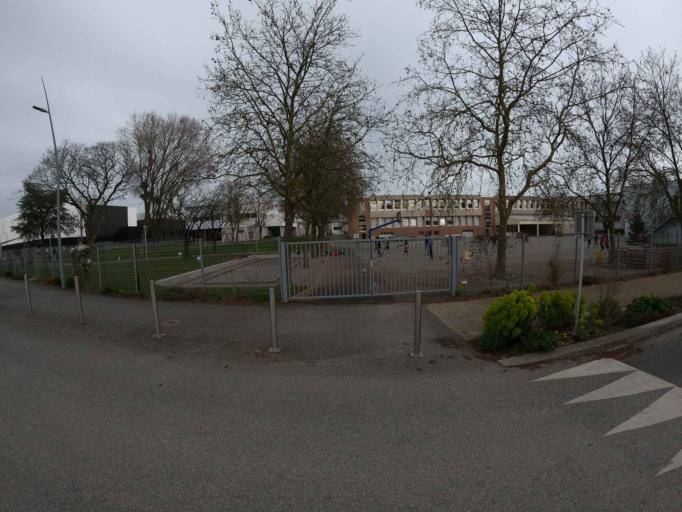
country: FR
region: Pays de la Loire
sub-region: Departement de la Vendee
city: Montaigu
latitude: 46.9824
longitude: -1.3093
